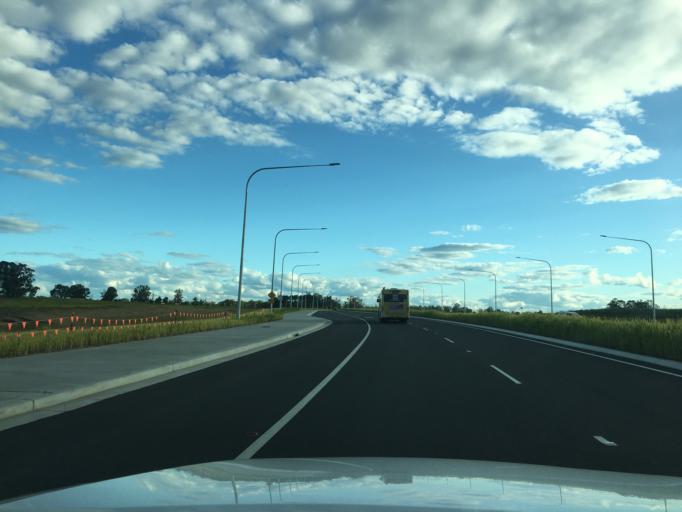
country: AU
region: New South Wales
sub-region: Liverpool
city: Bringelly
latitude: -33.8784
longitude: 150.7472
